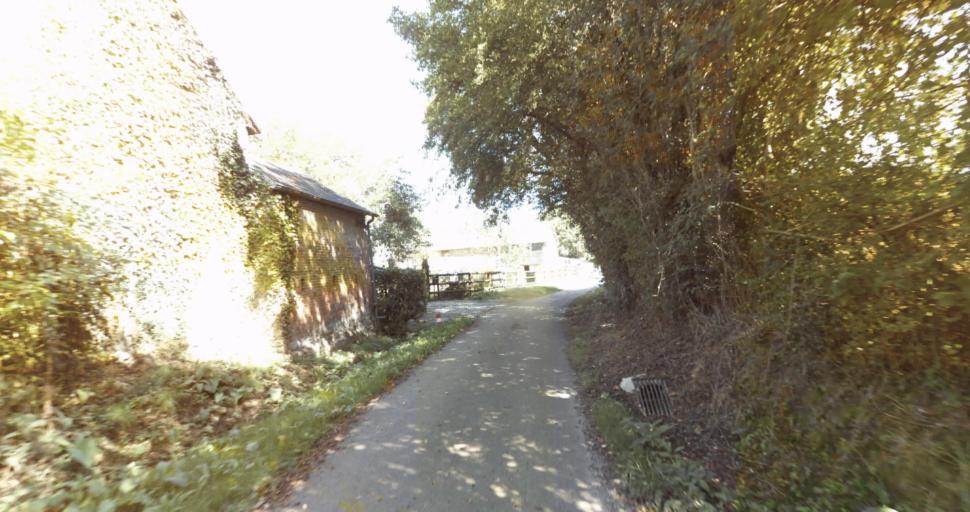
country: FR
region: Lower Normandy
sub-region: Departement de l'Orne
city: Gace
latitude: 48.7728
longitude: 0.2993
